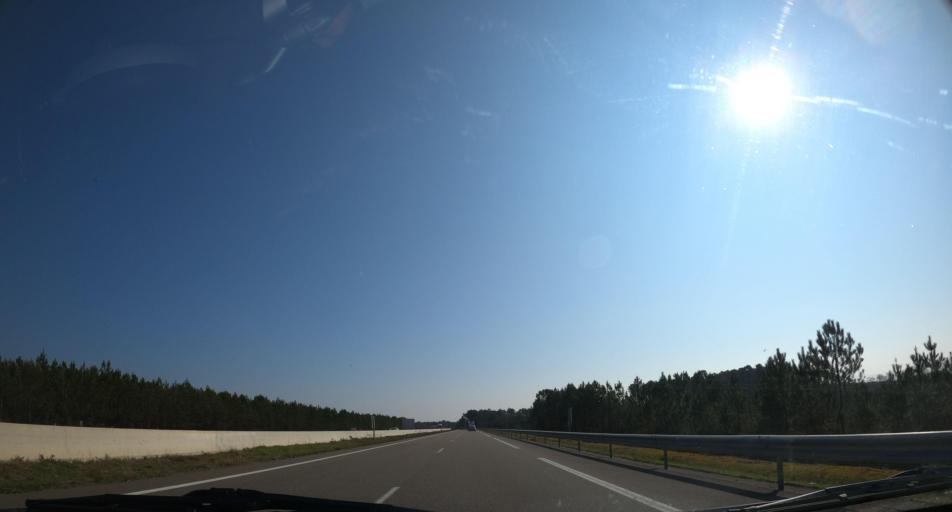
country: FR
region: Aquitaine
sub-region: Departement des Landes
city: Saint-Geours-de-Maremne
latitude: 43.6949
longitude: -1.2136
